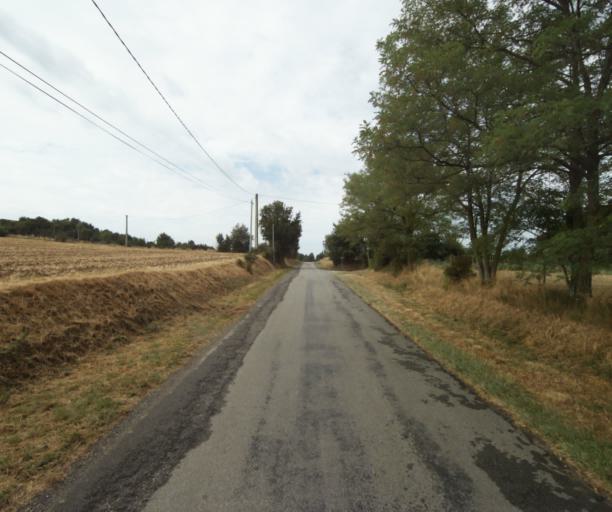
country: FR
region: Midi-Pyrenees
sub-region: Departement de la Haute-Garonne
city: Revel
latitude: 43.4445
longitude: 1.9755
